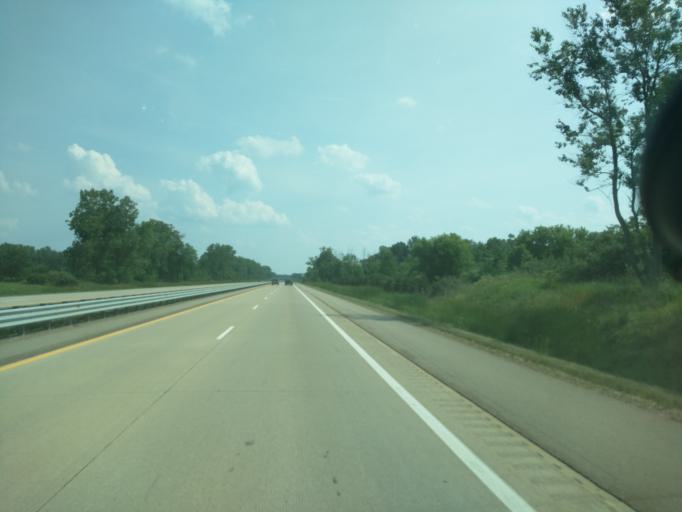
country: US
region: Michigan
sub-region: Jackson County
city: Jackson
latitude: 42.3389
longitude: -84.4290
